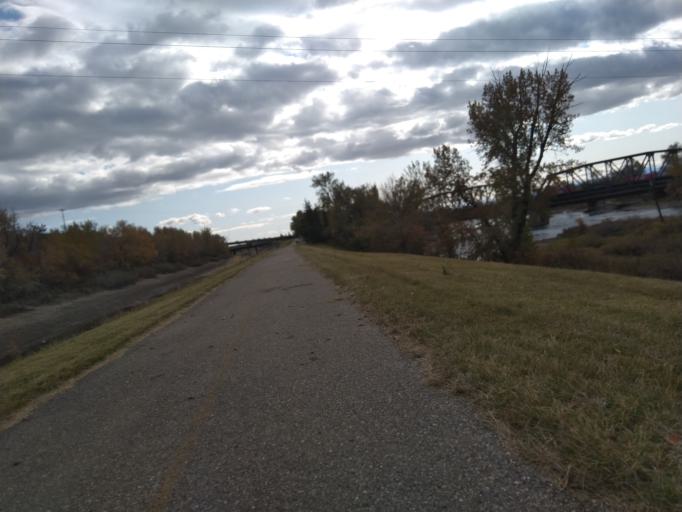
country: CA
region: Alberta
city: Calgary
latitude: 51.0164
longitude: -114.0096
